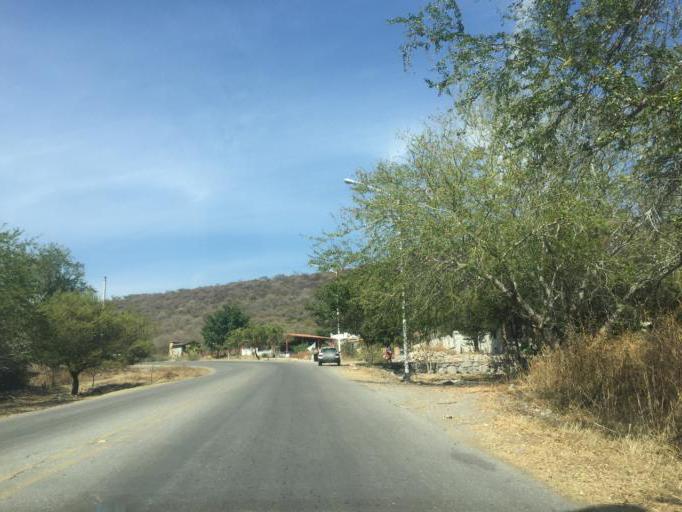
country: MX
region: Morelos
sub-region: Miacatlan
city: Xochicalco (Cirenio Longares)
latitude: 18.7922
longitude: -99.2970
